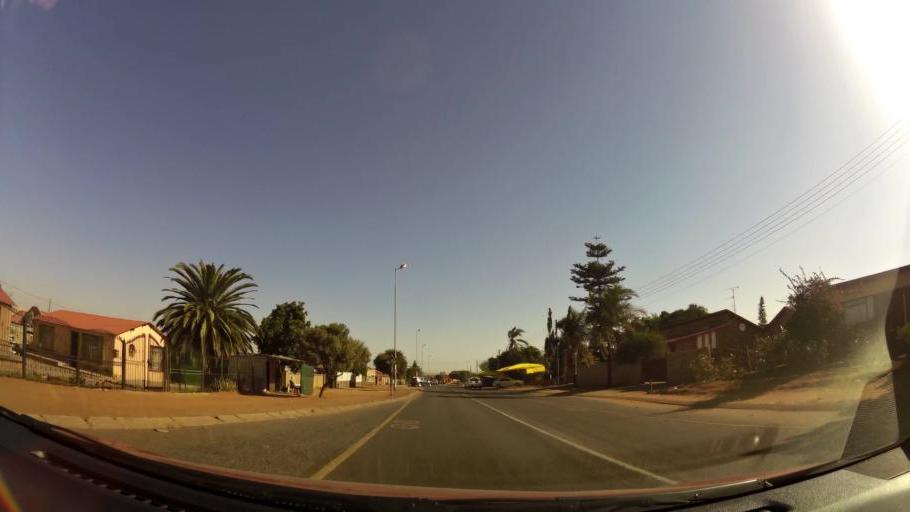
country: ZA
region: Gauteng
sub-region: City of Tshwane Metropolitan Municipality
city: Mabopane
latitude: -25.5434
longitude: 28.1020
